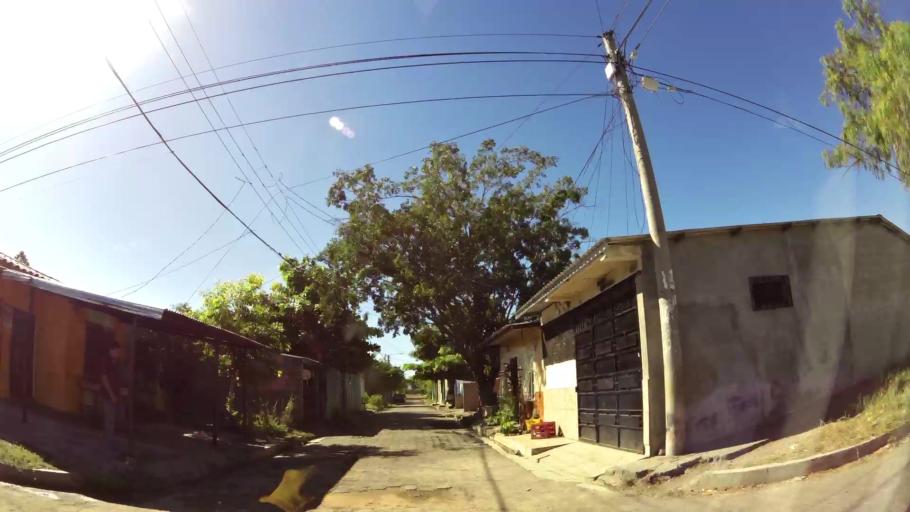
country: SV
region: San Miguel
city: San Miguel
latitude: 13.4712
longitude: -88.1549
